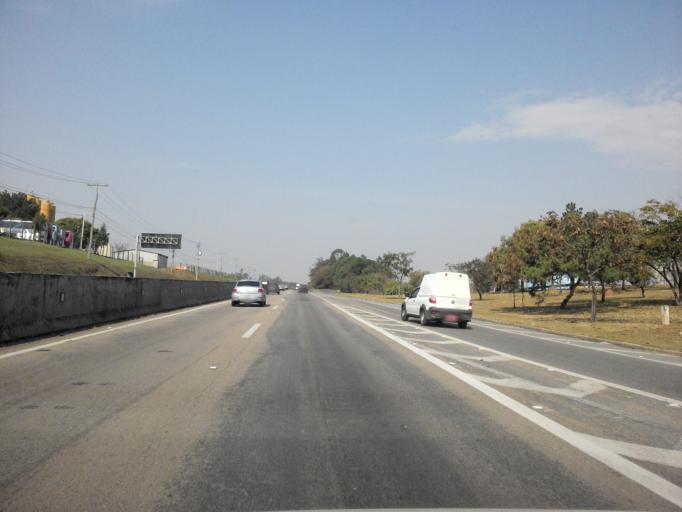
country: BR
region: Sao Paulo
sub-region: Hortolandia
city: Hortolandia
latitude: -22.8882
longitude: -47.1442
